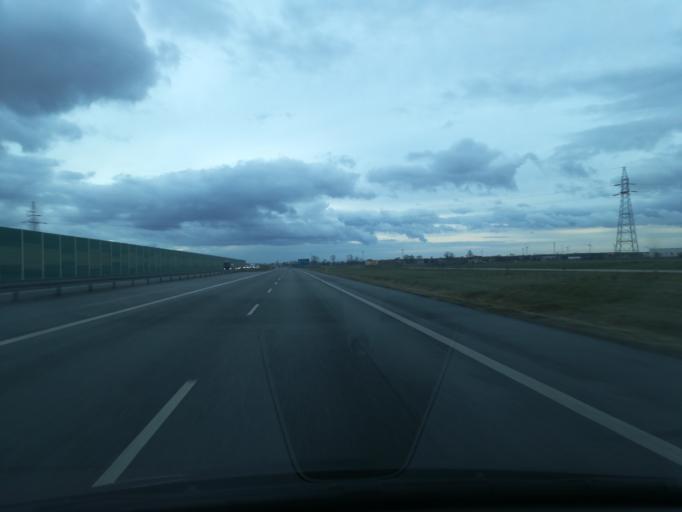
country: PL
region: Lodz Voivodeship
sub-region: Powiat kutnowski
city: Krzyzanow
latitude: 52.2420
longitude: 19.4504
